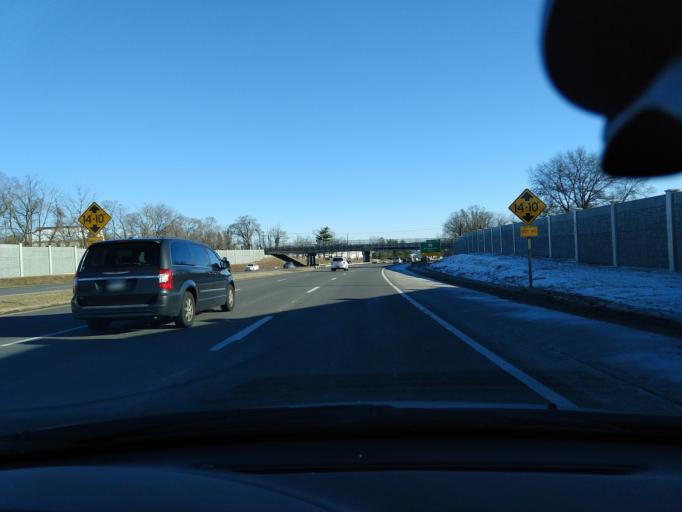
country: US
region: Virginia
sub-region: City of Roanoke
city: Roanoke
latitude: 37.2915
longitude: -79.9434
